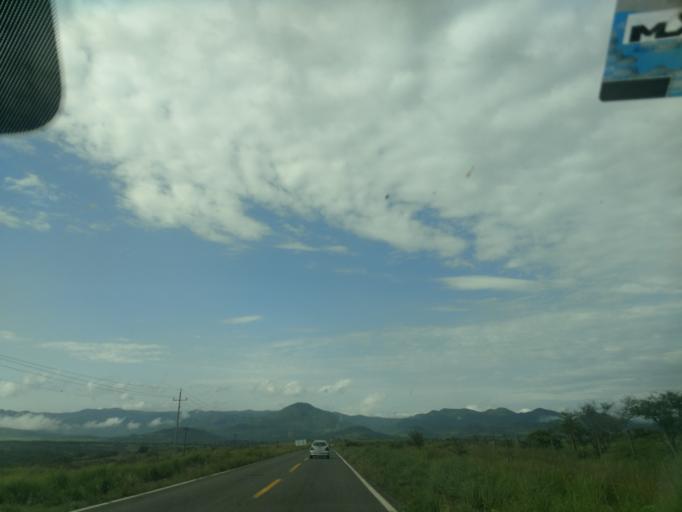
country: MX
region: Jalisco
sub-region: Atengo
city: Soyatlan del Oro
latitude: 20.5409
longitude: -104.3103
